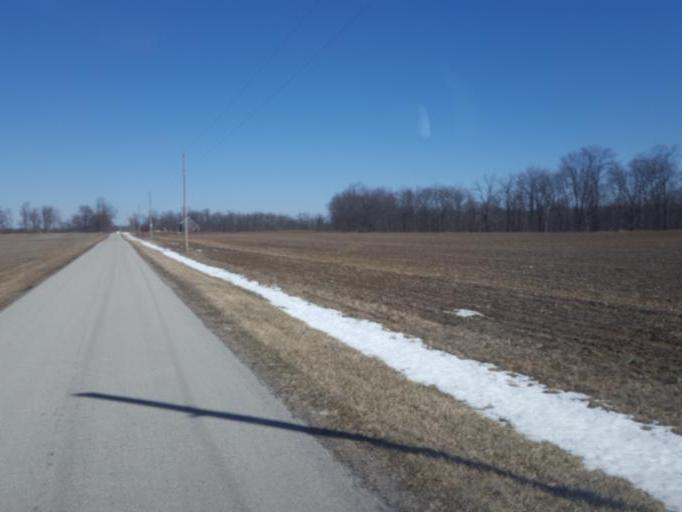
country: US
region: Ohio
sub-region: Wyandot County
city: Upper Sandusky
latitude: 40.7543
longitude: -83.1450
